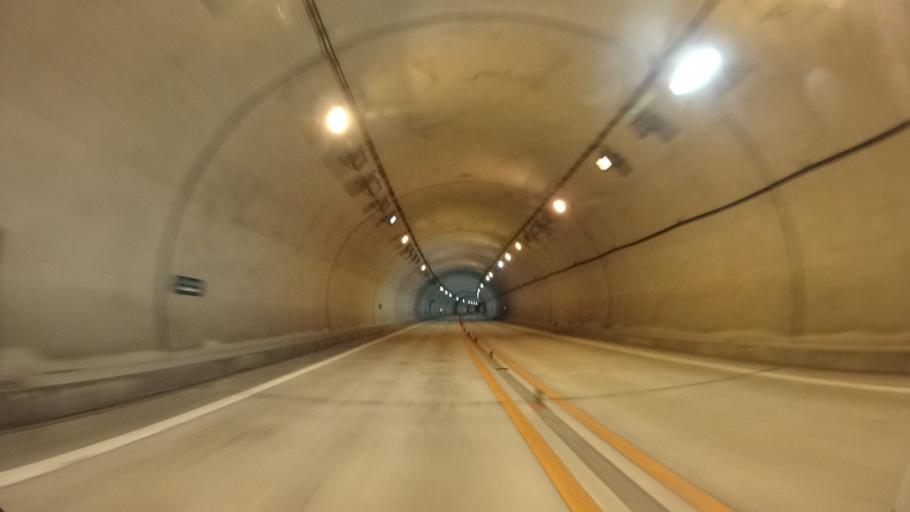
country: JP
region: Hyogo
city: Yamazakicho-nakabirose
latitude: 35.1076
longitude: 134.3302
